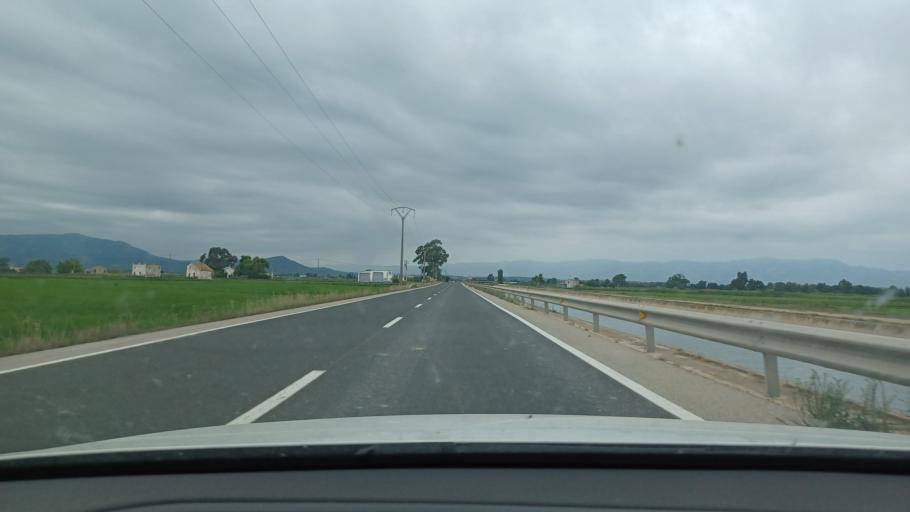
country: ES
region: Catalonia
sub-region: Provincia de Tarragona
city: Deltebre
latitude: 40.7106
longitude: 0.6641
